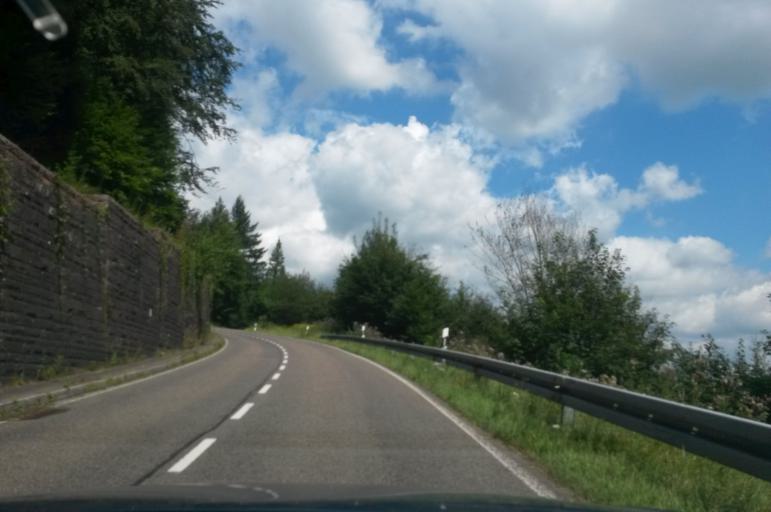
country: DE
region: Baden-Wuerttemberg
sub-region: Karlsruhe Region
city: Bad Herrenalb
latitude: 48.8616
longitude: 8.4455
